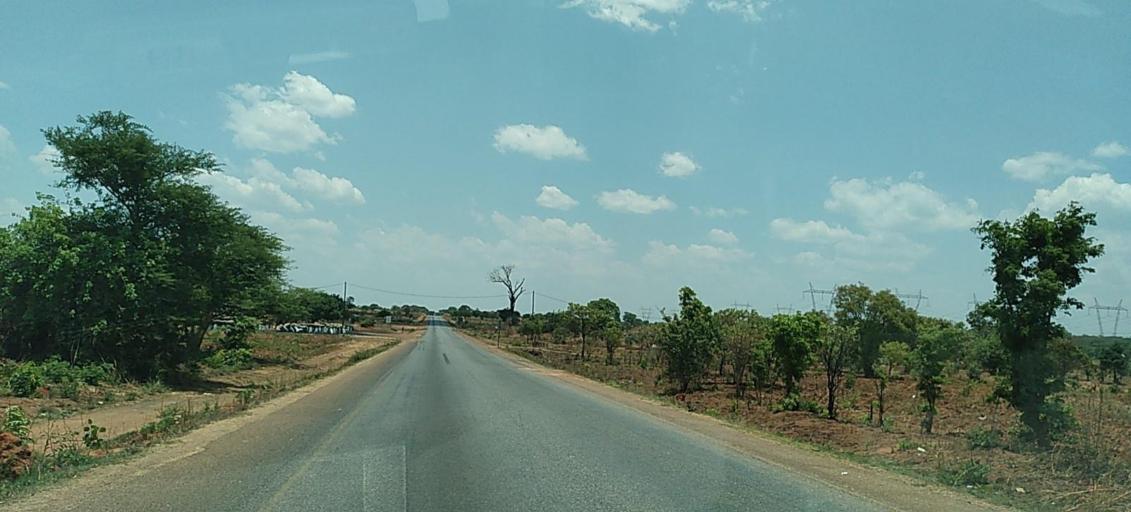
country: ZM
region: Central
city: Kapiri Mposhi
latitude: -13.7008
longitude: 28.6289
